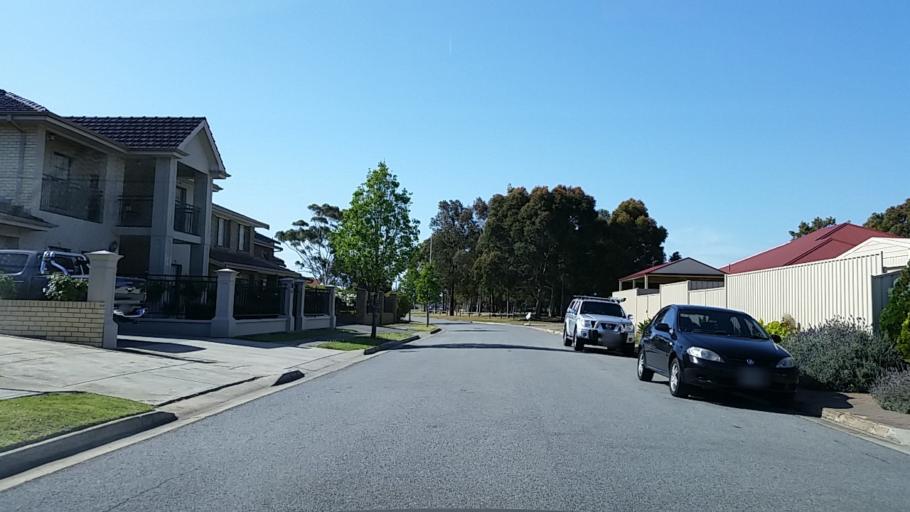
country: AU
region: South Australia
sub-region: Charles Sturt
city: Henley Beach
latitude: -34.9189
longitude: 138.5086
